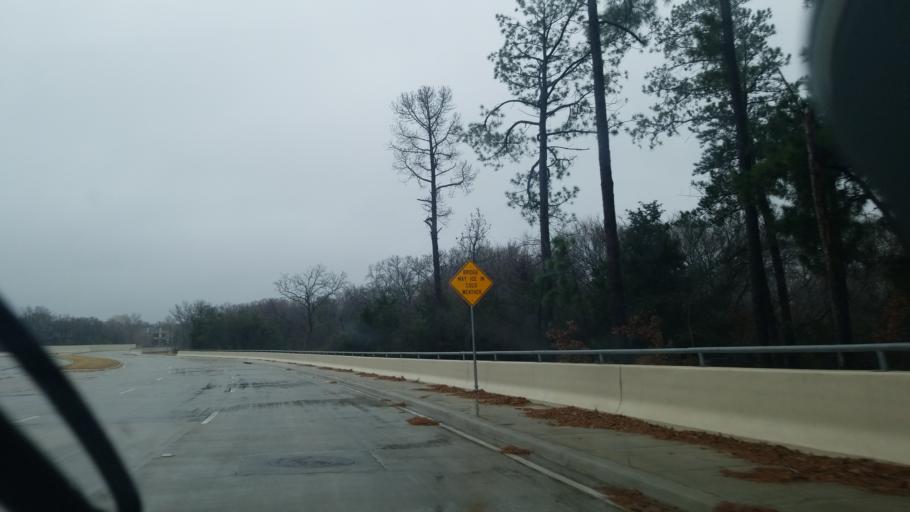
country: US
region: Texas
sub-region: Denton County
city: Corinth
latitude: 33.1377
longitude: -97.0960
